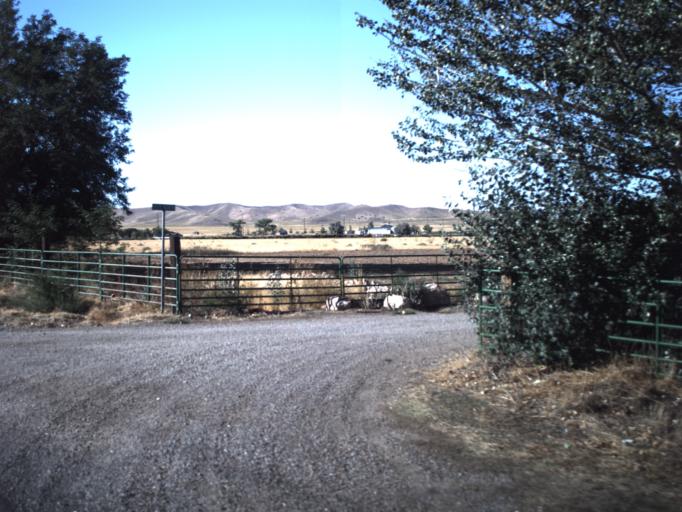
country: US
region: Utah
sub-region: Millard County
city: Delta
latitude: 39.4758
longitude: -112.2688
